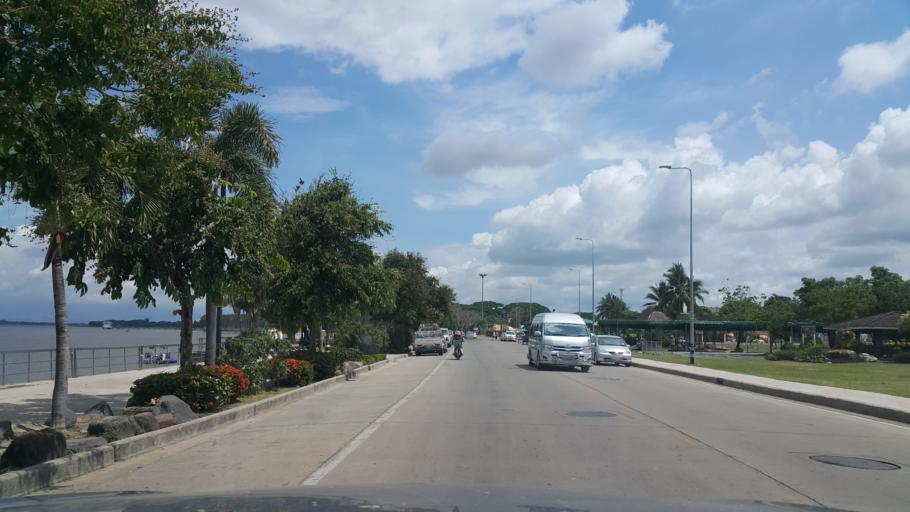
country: TH
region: Phayao
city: Phayao
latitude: 19.1692
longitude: 99.8954
